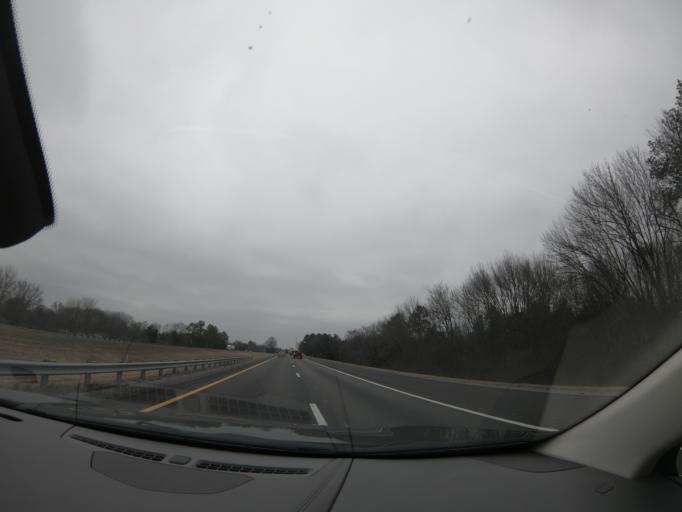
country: US
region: Tennessee
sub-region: Rutherford County
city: Plainview
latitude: 35.7598
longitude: -86.3514
